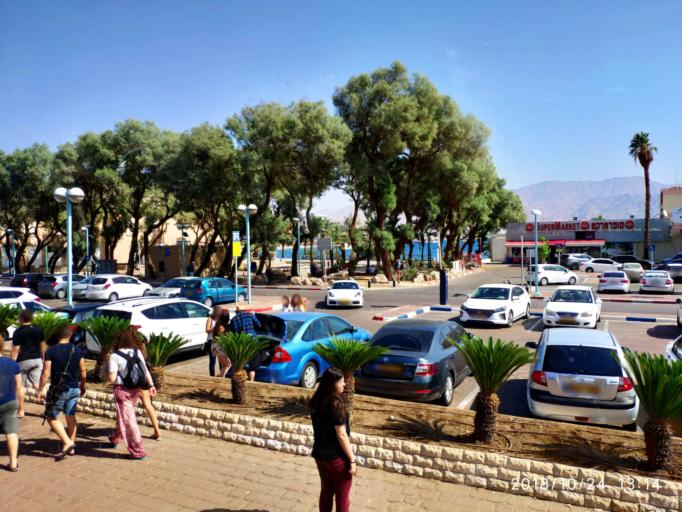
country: IL
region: Southern District
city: Eilat
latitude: 29.5490
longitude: 34.9525
